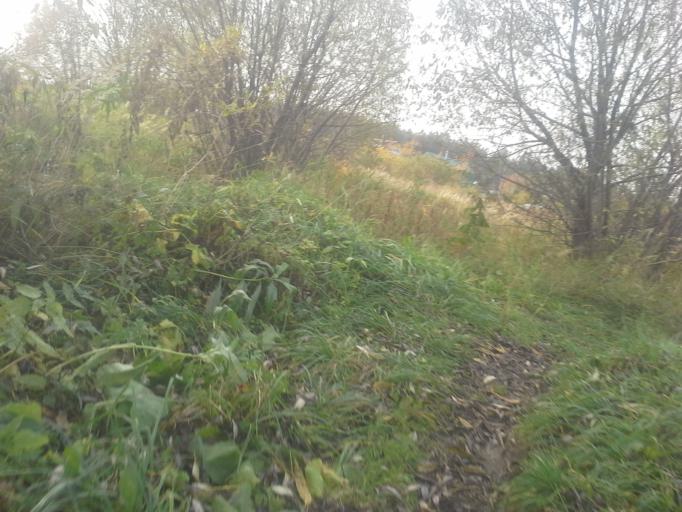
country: RU
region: Moskovskaya
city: Golitsyno
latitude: 55.5978
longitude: 36.9995
